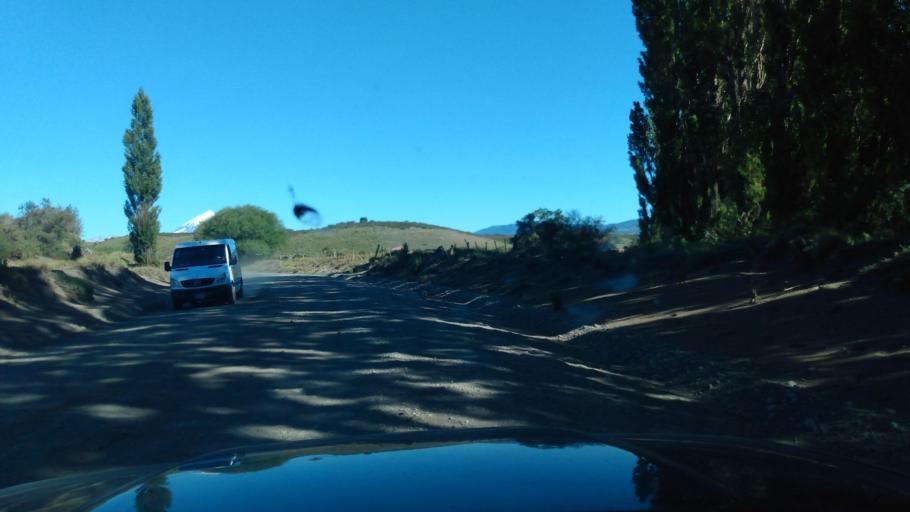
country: AR
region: Neuquen
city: Junin de los Andes
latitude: -39.8291
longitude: -71.1931
